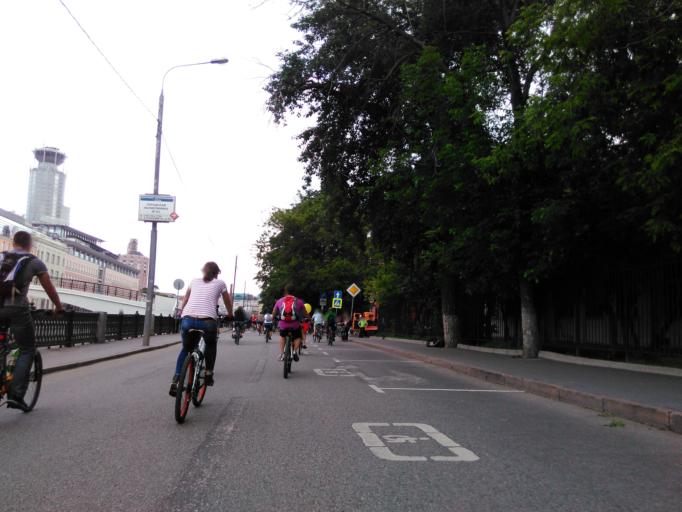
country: RU
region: Moscow
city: Zamoskvorech'ye
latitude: 55.7372
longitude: 37.6390
